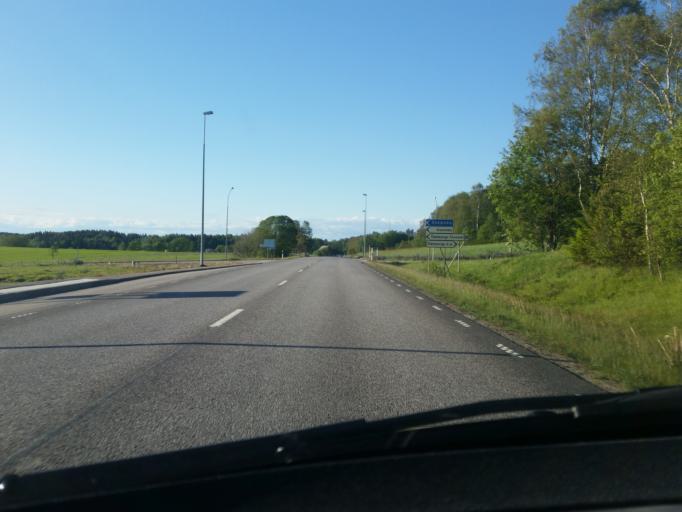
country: SE
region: Vaestra Goetaland
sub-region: Fargelanda Kommun
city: Faergelanda
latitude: 58.5419
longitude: 11.9882
